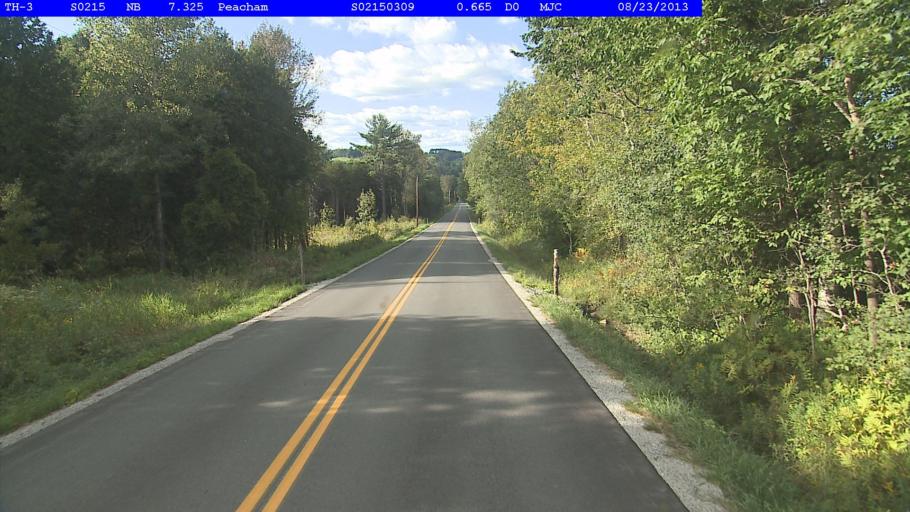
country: US
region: Vermont
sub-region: Caledonia County
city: Saint Johnsbury
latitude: 44.3074
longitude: -72.1653
